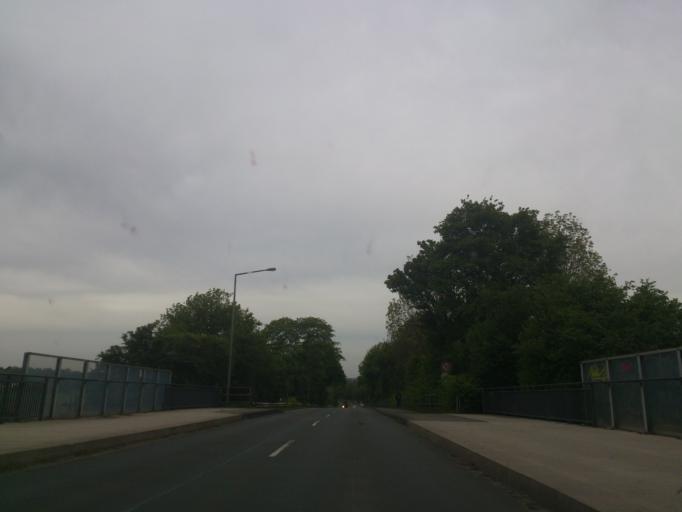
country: DE
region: North Rhine-Westphalia
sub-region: Regierungsbezirk Detmold
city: Paderborn
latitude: 51.7181
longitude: 8.7914
